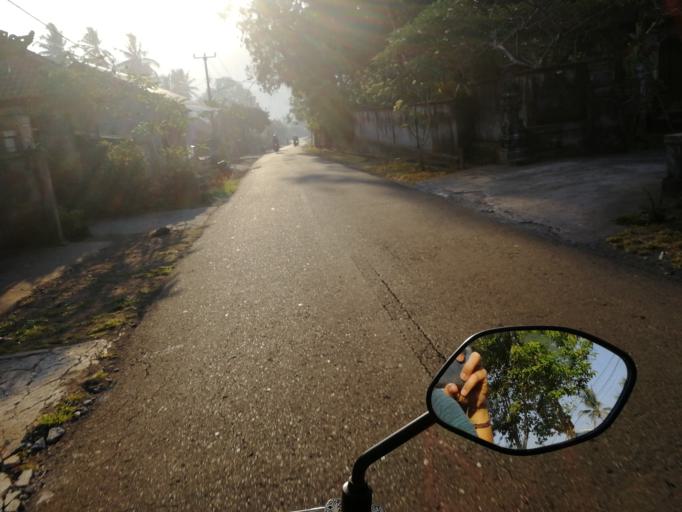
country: ID
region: Bali
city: Tistagede
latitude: -8.3859
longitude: 115.6101
